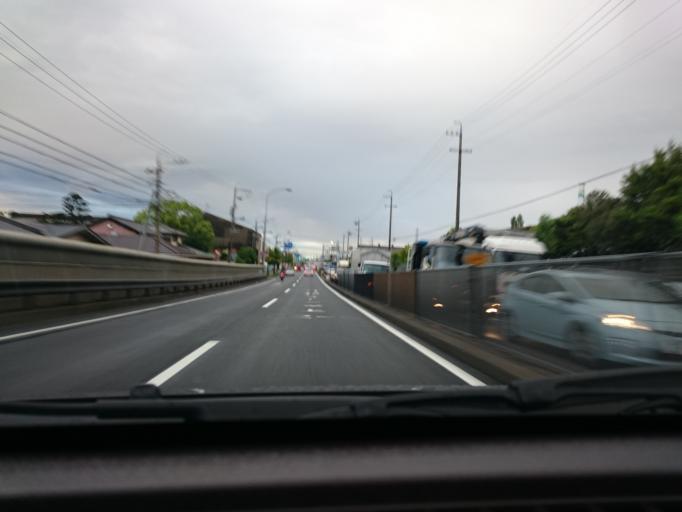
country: JP
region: Mie
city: Yokkaichi
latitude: 34.9695
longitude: 136.6386
